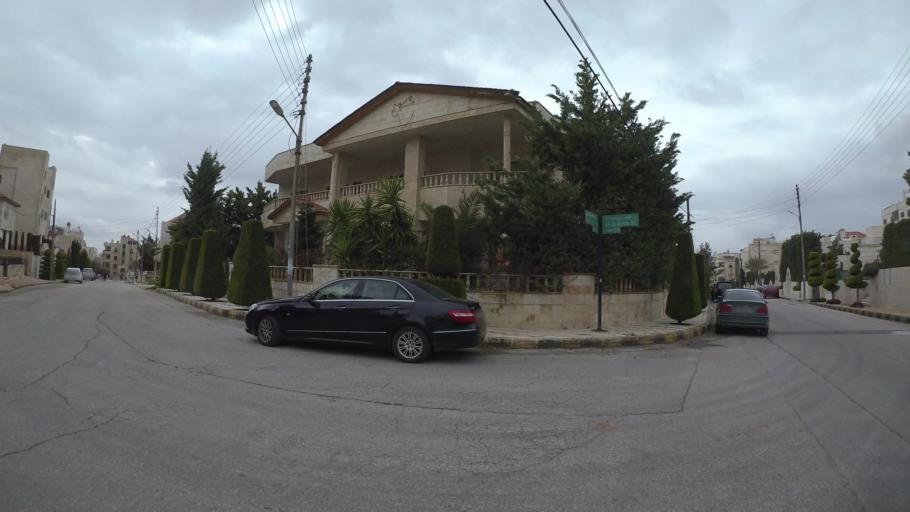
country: JO
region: Amman
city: Wadi as Sir
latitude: 31.9677
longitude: 35.8336
